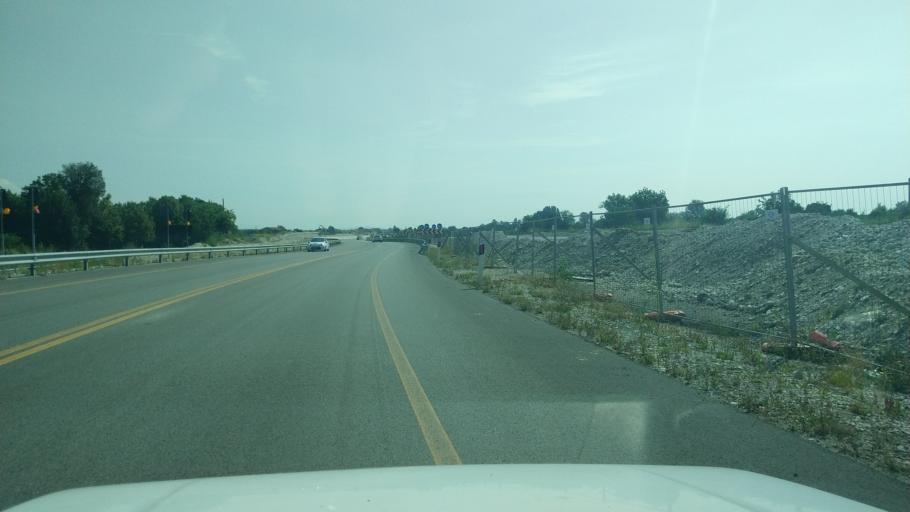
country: IT
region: Veneto
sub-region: Provincia di Vicenza
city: Nove
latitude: 45.7361
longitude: 11.6773
